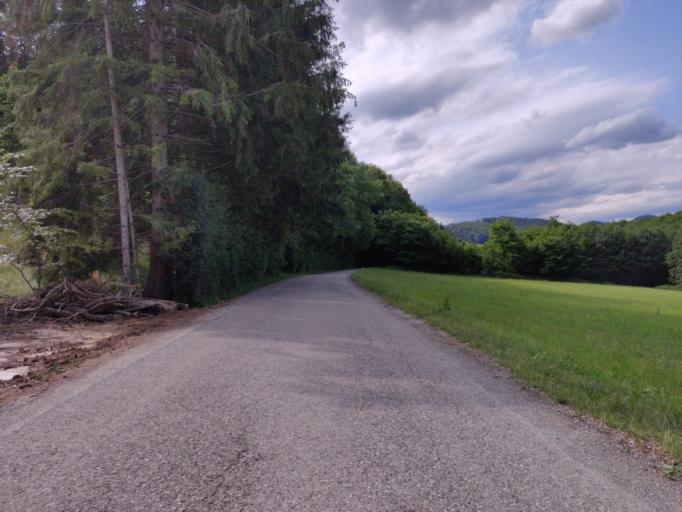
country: AT
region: Styria
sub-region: Politischer Bezirk Graz-Umgebung
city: Thal
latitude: 47.0642
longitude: 15.3425
